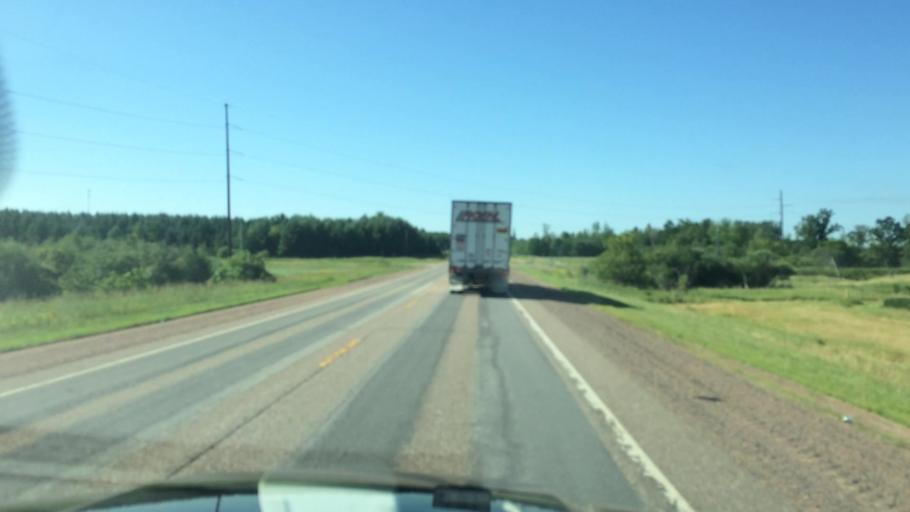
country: US
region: Wisconsin
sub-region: Marathon County
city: Athens
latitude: 44.9324
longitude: -90.0790
